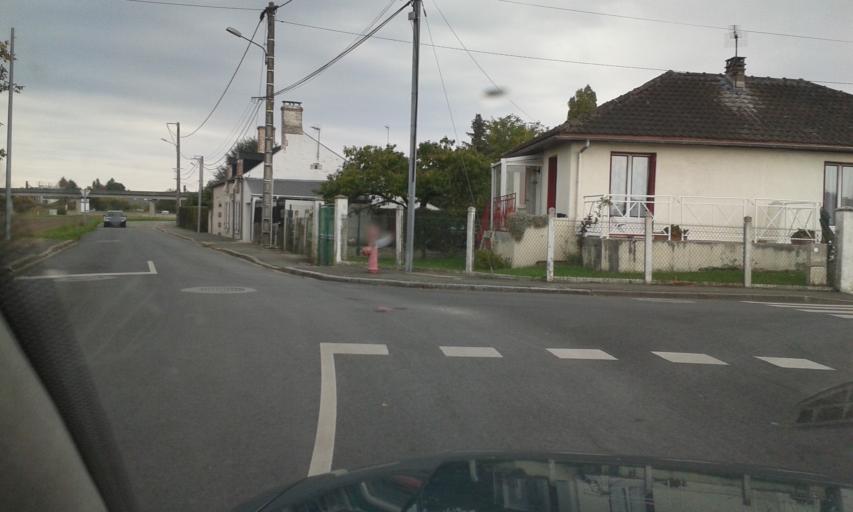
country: FR
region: Centre
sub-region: Departement du Loiret
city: Saran
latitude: 47.9869
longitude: 1.8878
